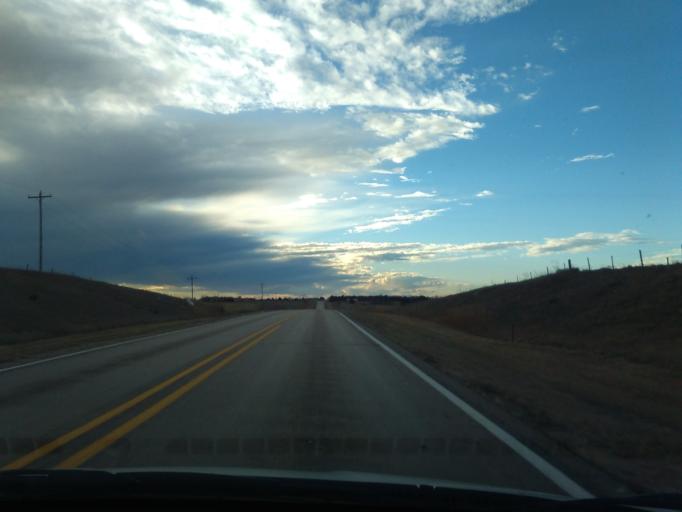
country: US
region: Nebraska
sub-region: Phelps County
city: Holdrege
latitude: 40.3072
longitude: -99.3535
